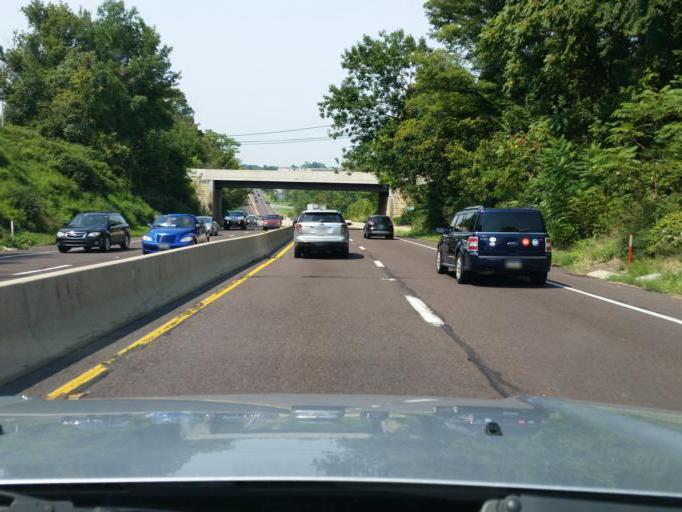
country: US
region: Pennsylvania
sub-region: Dauphin County
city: Hummelstown
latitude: 40.2609
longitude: -76.7239
